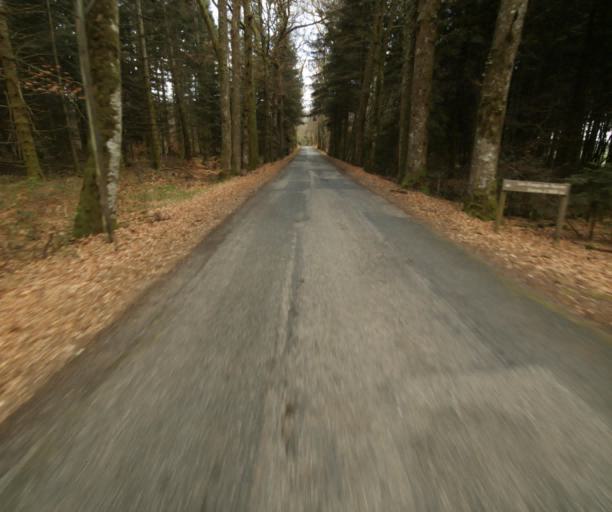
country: FR
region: Limousin
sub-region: Departement de la Correze
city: Correze
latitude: 45.2614
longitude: 1.9082
